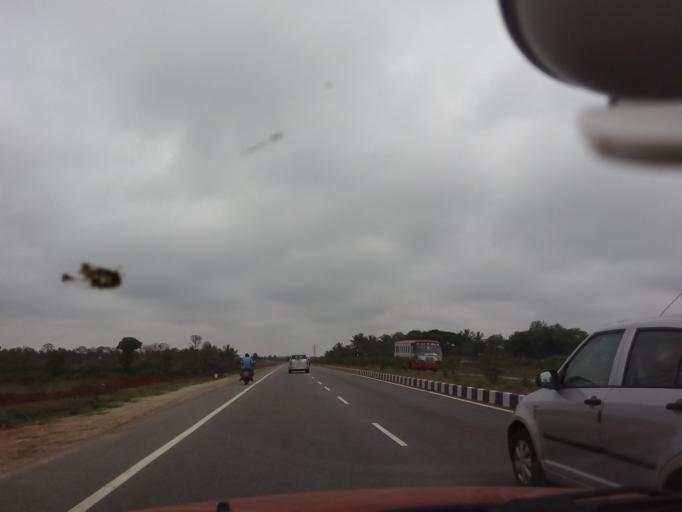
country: IN
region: Karnataka
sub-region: Hassan
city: Shravanabelagola
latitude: 12.9346
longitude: 76.5330
